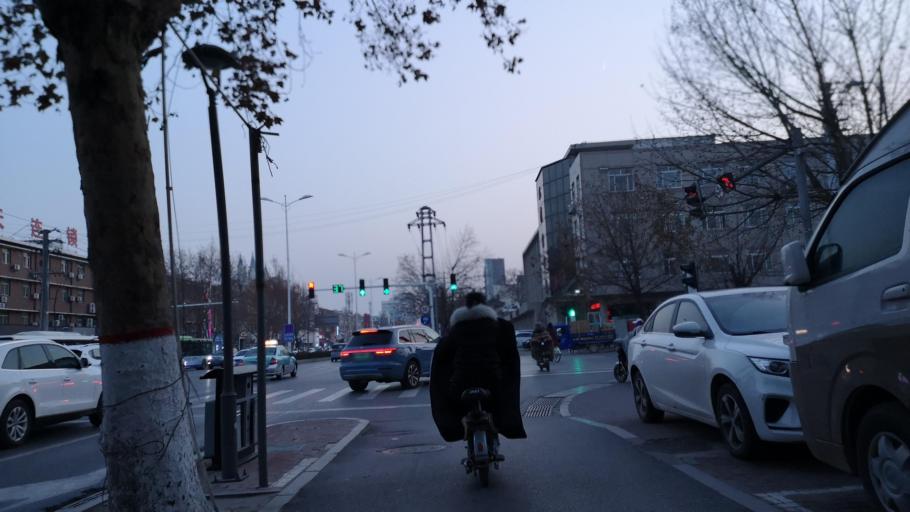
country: CN
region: Henan Sheng
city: Zhongyuanlu
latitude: 35.7734
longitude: 115.0698
